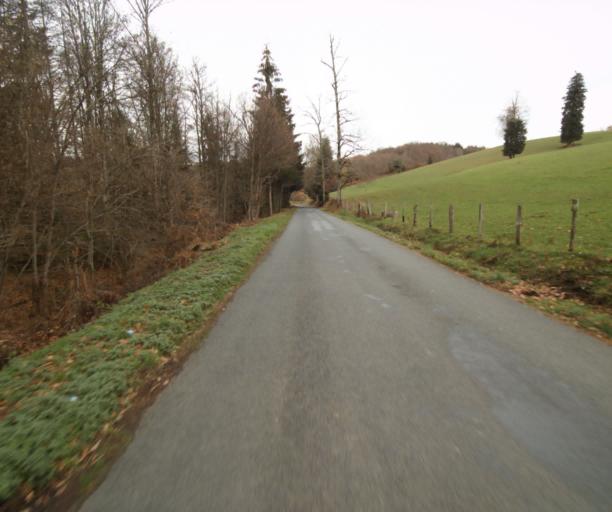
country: FR
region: Limousin
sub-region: Departement de la Correze
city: Chameyrat
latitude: 45.2594
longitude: 1.6781
